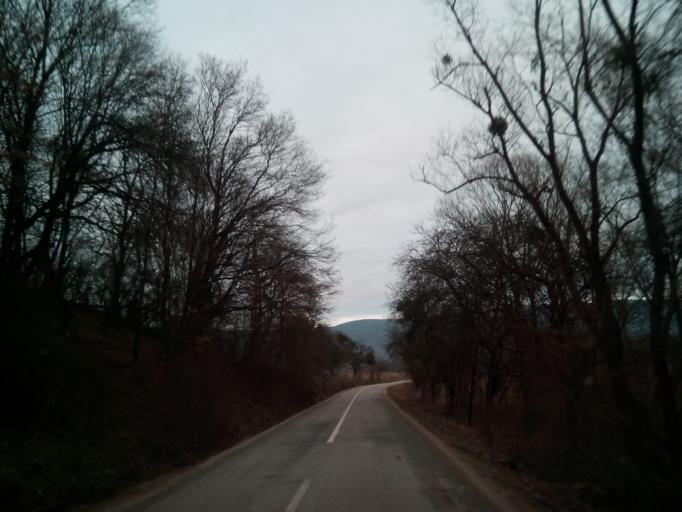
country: SK
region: Kosicky
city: Roznava
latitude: 48.5696
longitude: 20.6385
